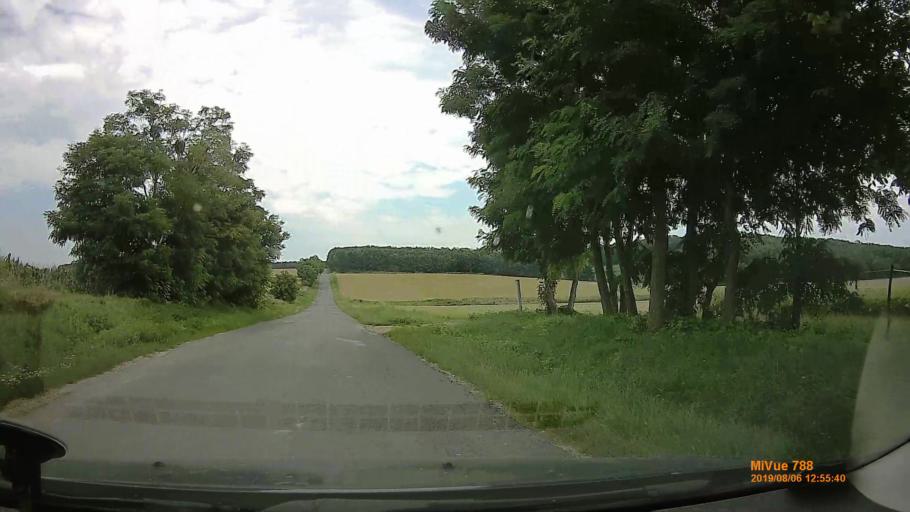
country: HU
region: Zala
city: Pacsa
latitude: 46.6361
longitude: 17.0193
